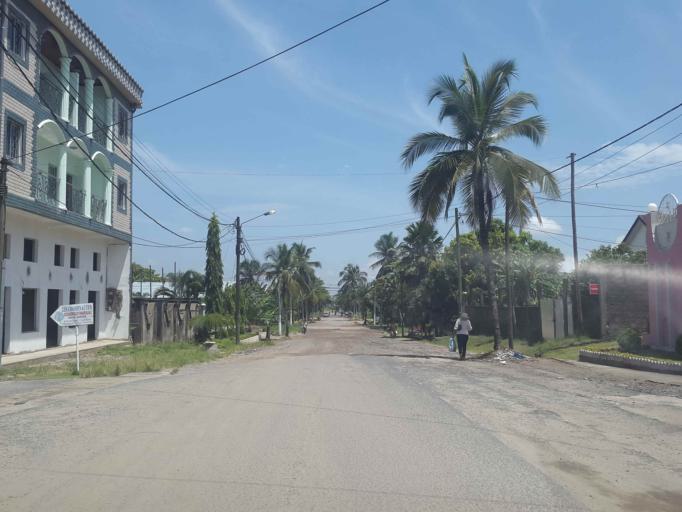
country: CM
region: Littoral
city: Douala
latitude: 4.0925
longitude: 9.7340
